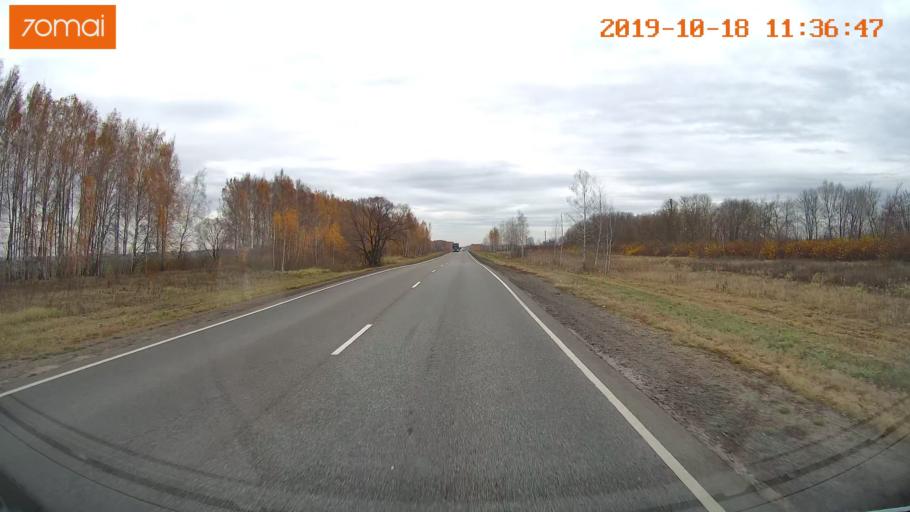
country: RU
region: Rjazan
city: Oktyabr'skiy
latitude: 54.1446
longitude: 38.8150
